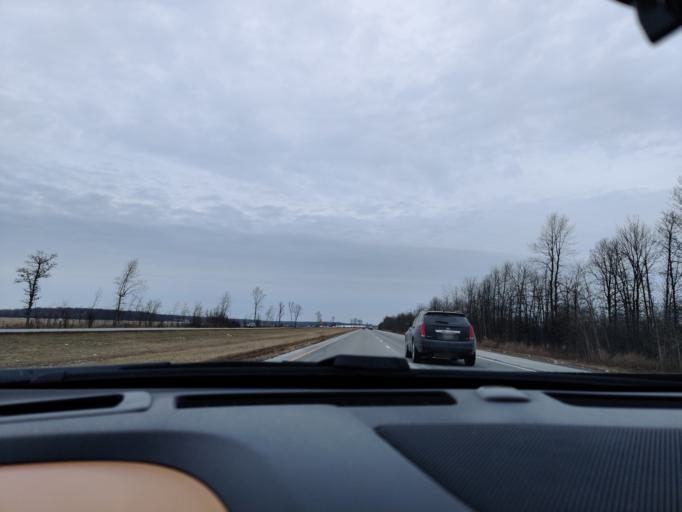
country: US
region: New York
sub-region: St. Lawrence County
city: Norfolk
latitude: 44.9007
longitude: -75.2372
